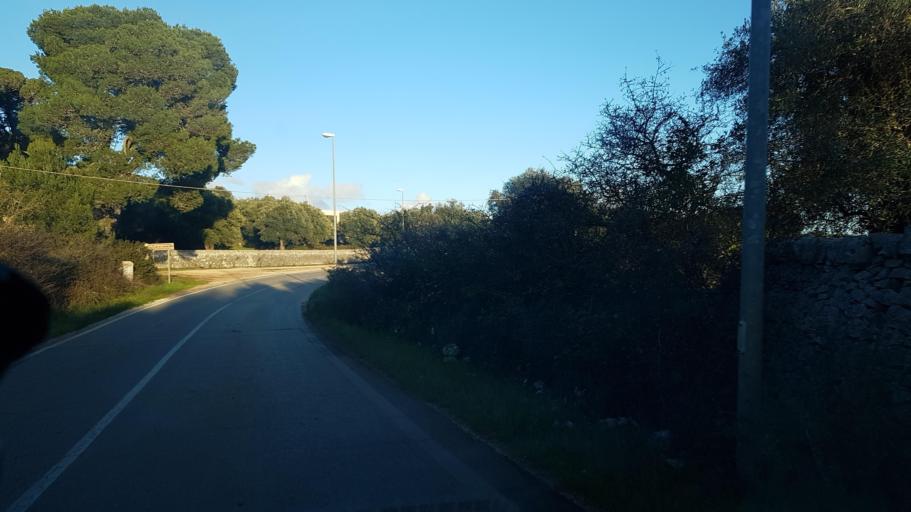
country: IT
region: Apulia
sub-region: Provincia di Brindisi
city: Ostuni
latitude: 40.7074
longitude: 17.5367
